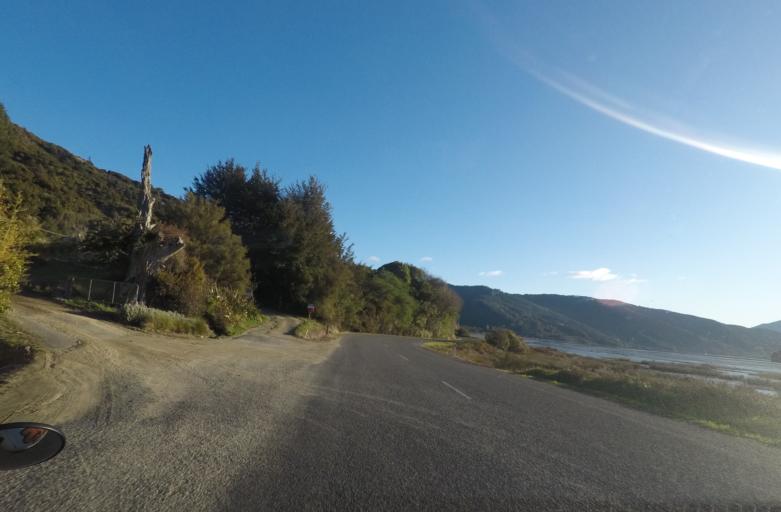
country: NZ
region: Marlborough
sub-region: Marlborough District
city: Picton
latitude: -41.2906
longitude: 173.8455
